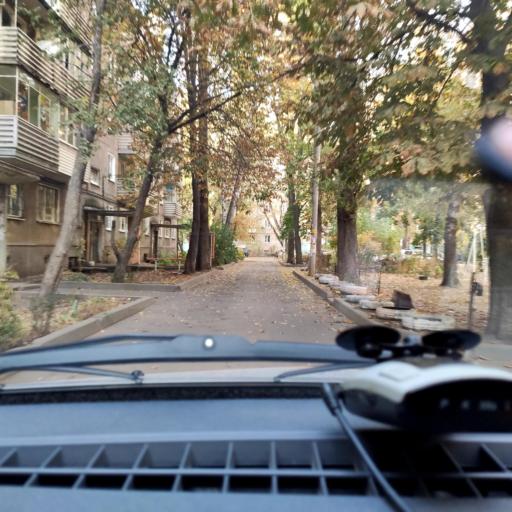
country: RU
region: Voronezj
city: Voronezh
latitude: 51.7020
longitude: 39.1913
